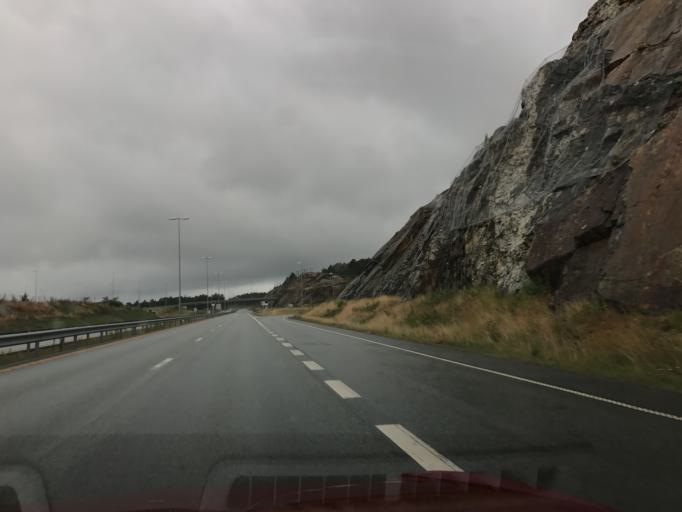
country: NO
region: Aust-Agder
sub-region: Lillesand
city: Lillesand
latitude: 58.2707
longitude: 8.3974
